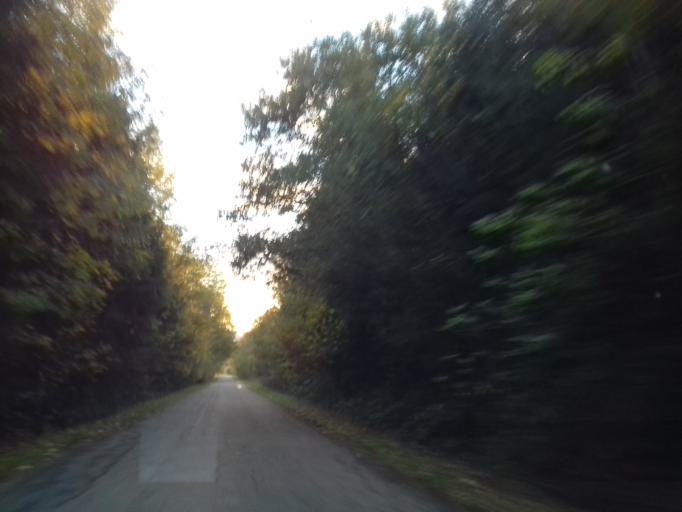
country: CZ
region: Pardubicky
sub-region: Okres Chrudim
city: Skutec
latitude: 49.8220
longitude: 15.9640
